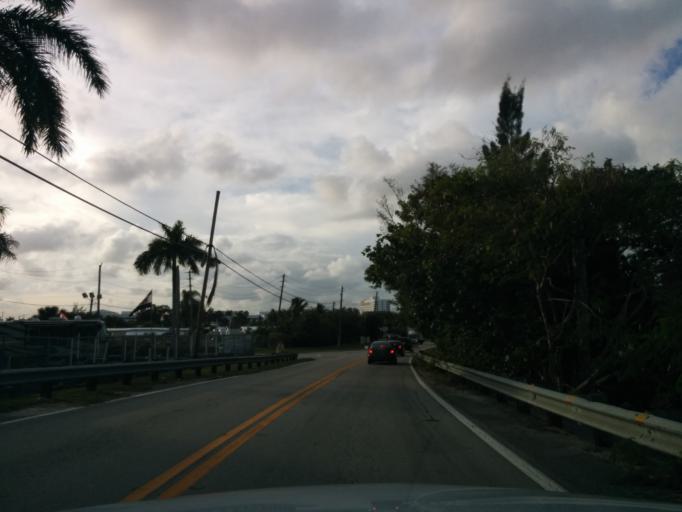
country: US
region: Florida
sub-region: Broward County
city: Dania Beach
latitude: 26.0594
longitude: -80.1553
